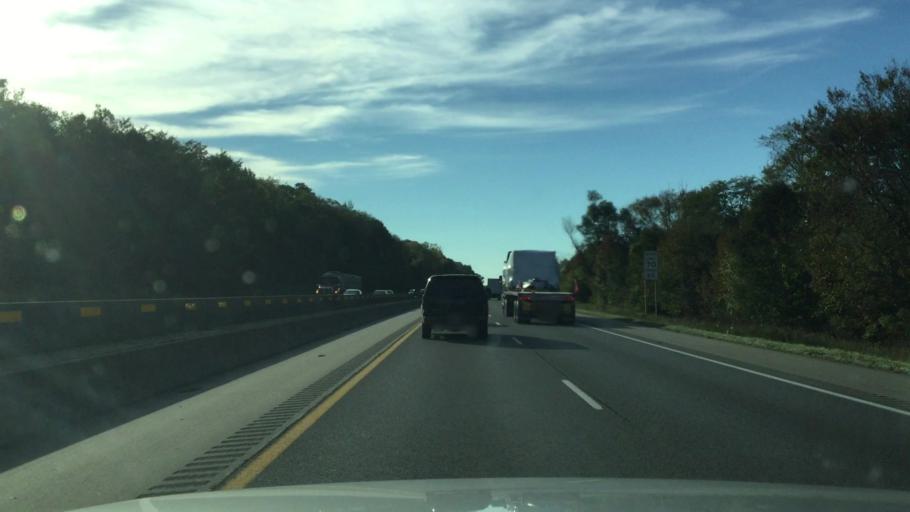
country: US
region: Michigan
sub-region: Kalamazoo County
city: Galesburg
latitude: 42.2694
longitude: -85.4588
